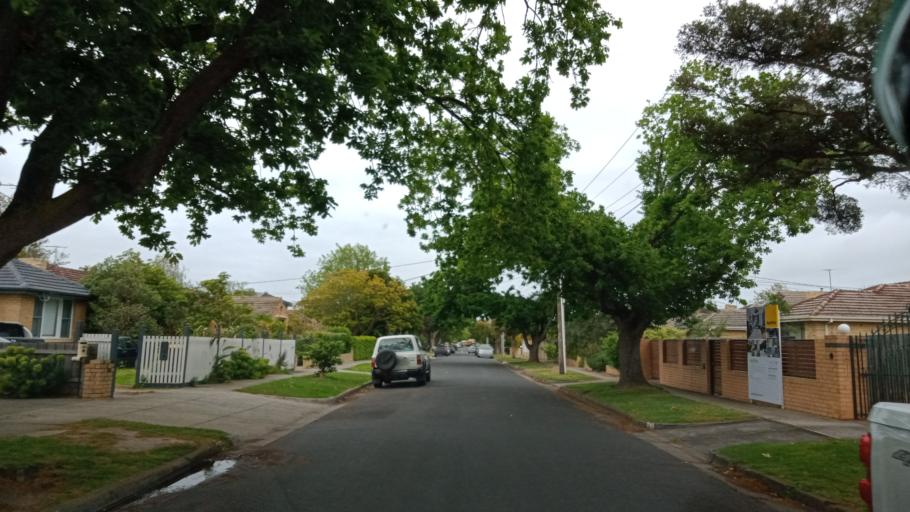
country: AU
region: Victoria
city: McKinnon
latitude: -37.9311
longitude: 145.0675
